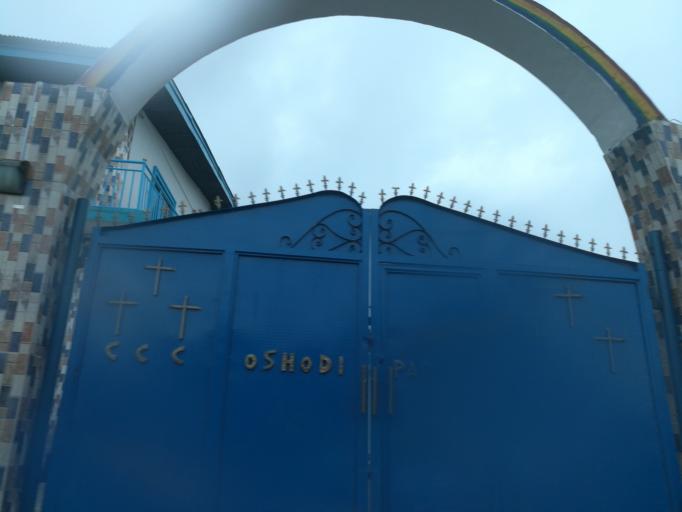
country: NG
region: Lagos
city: Oshodi
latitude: 6.5660
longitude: 3.3425
